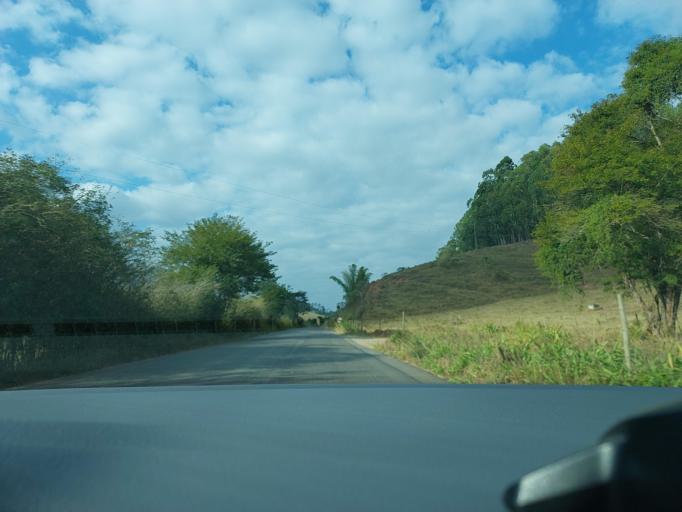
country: BR
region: Minas Gerais
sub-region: Vicosa
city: Vicosa
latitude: -20.8306
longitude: -42.7539
